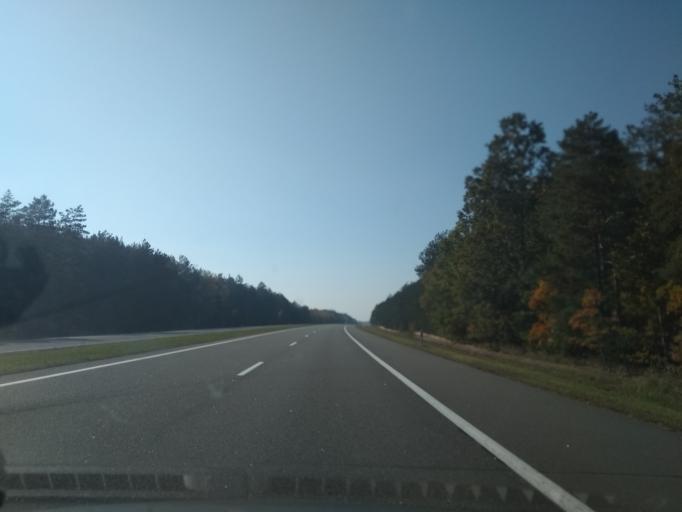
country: BY
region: Brest
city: Antopal'
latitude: 52.3632
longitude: 24.7254
